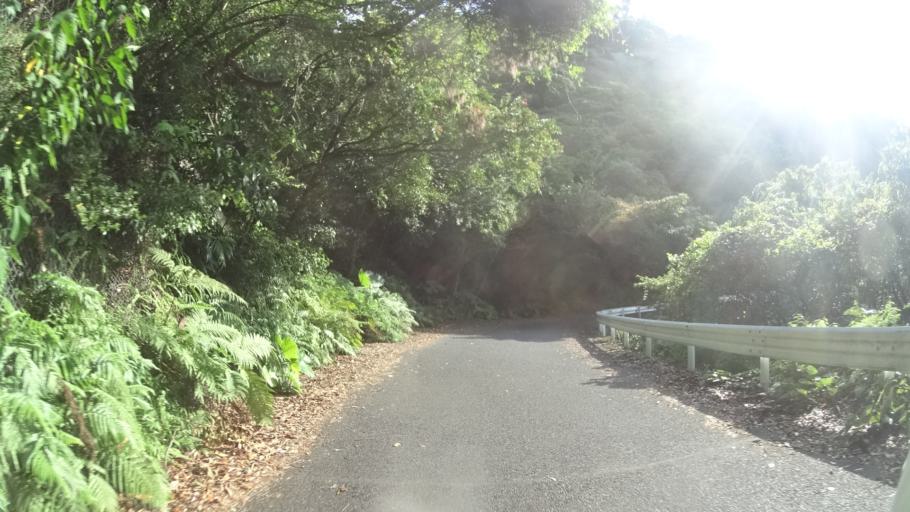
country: JP
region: Kagoshima
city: Nishinoomote
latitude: 30.3816
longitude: 130.3818
